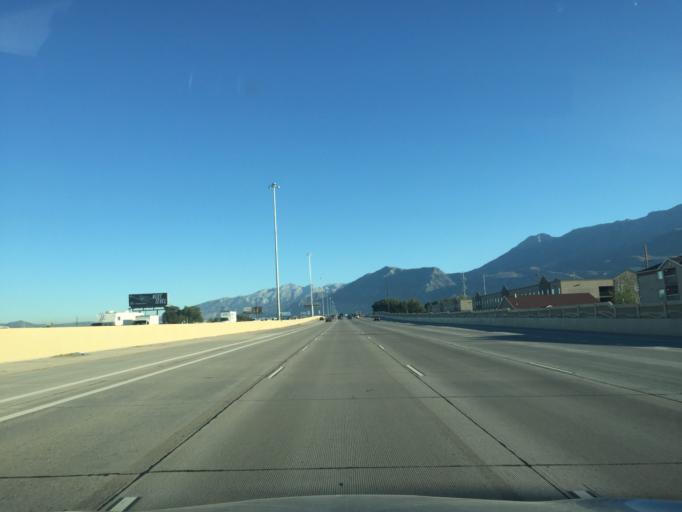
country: US
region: Utah
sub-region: Utah County
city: Orem
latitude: 40.2863
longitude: -111.7254
